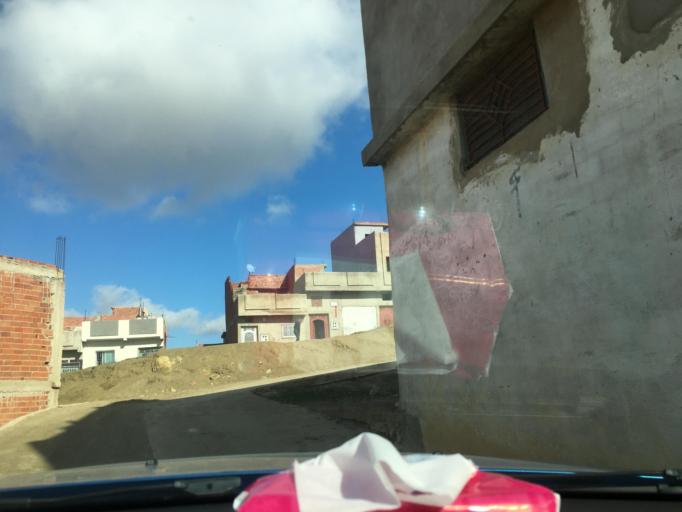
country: MA
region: Tanger-Tetouan
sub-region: Tanger-Assilah
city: Tangier
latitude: 35.7145
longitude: -5.8149
